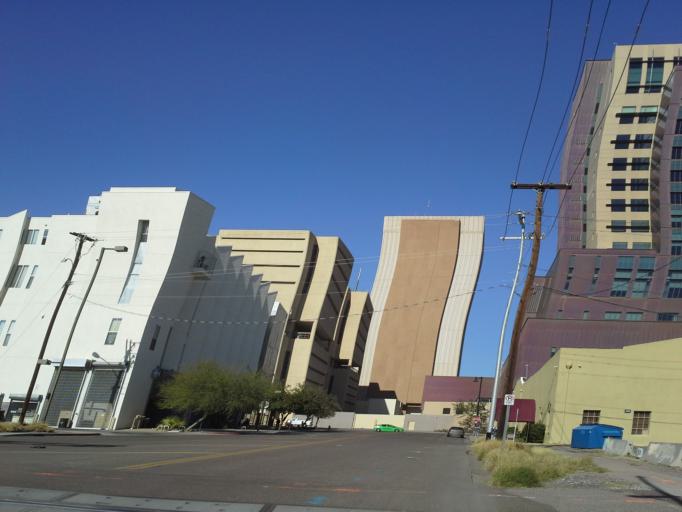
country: US
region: Arizona
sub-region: Maricopa County
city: Phoenix
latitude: 33.4441
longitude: -112.0763
